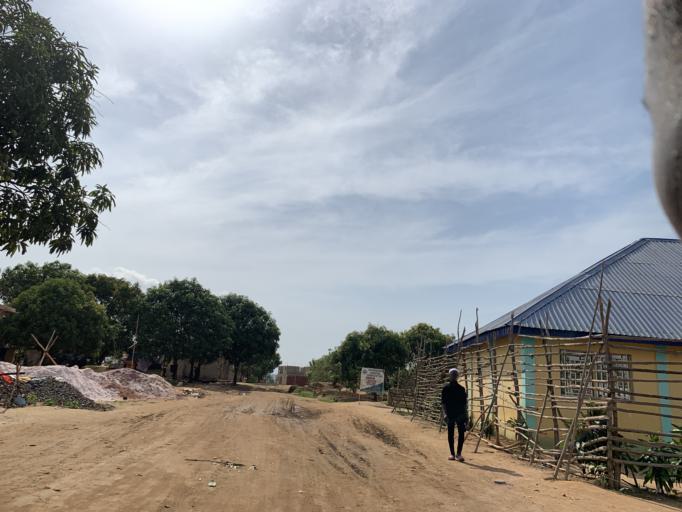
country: SL
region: Western Area
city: Waterloo
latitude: 8.3459
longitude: -13.0509
